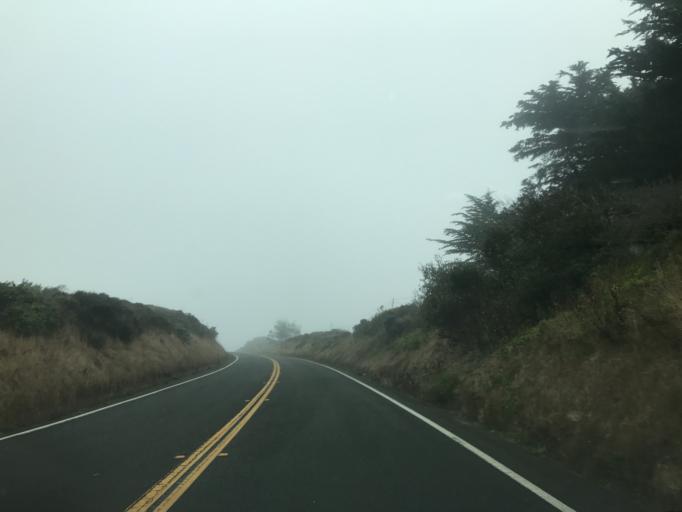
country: US
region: California
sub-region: Mendocino County
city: Boonville
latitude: 38.9969
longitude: -123.6895
